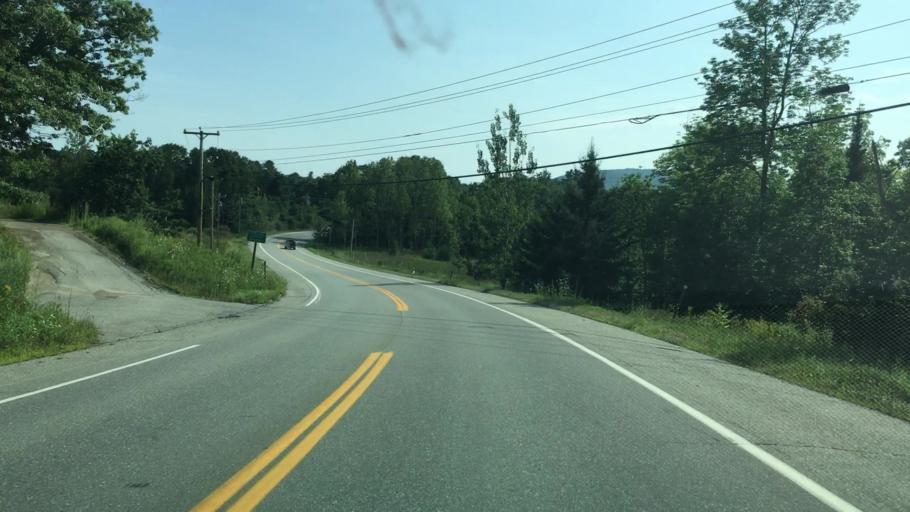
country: US
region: Maine
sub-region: Waldo County
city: Frankfort
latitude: 44.6266
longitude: -68.8689
